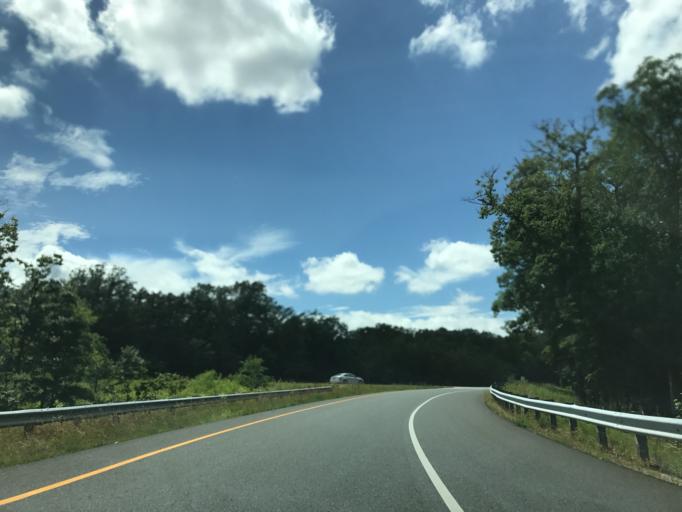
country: US
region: Maryland
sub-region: Howard County
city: North Laurel
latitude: 39.1324
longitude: -76.8638
